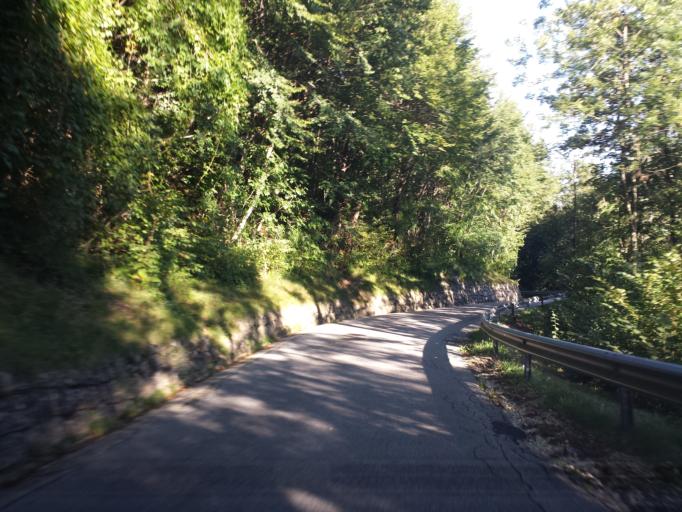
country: IT
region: Veneto
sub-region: Provincia di Vicenza
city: Recoaro Terme
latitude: 45.7166
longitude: 11.1903
